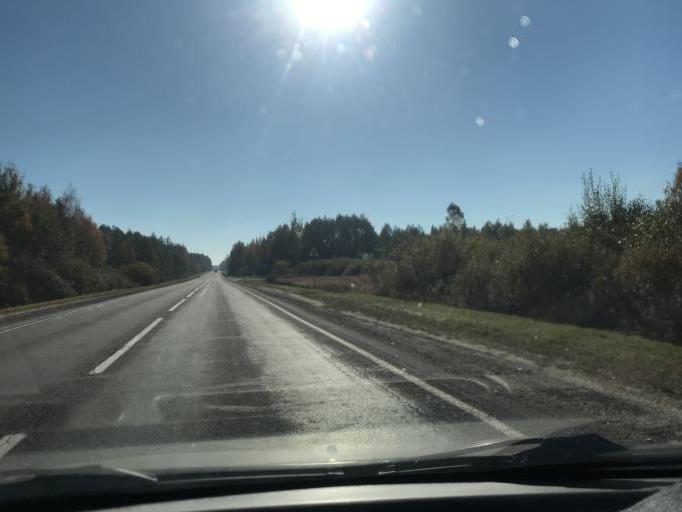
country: BY
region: Gomel
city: Kastsyukowka
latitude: 52.4401
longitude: 30.8257
